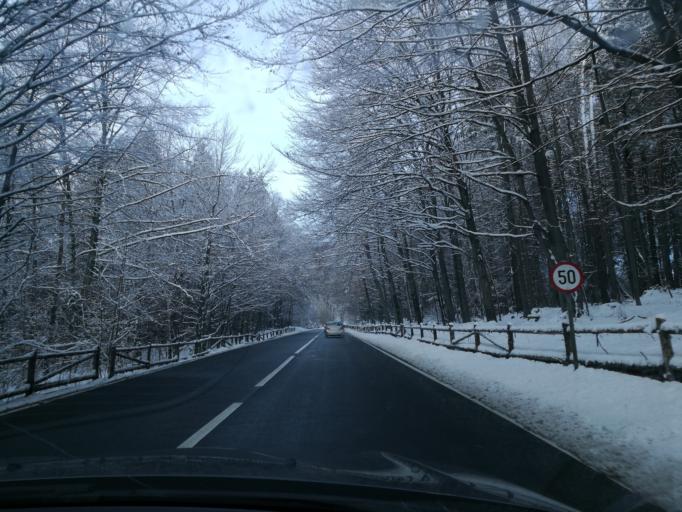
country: RO
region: Brasov
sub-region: Comuna Ghimbav
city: Ghimbav
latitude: 45.6179
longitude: 25.5446
